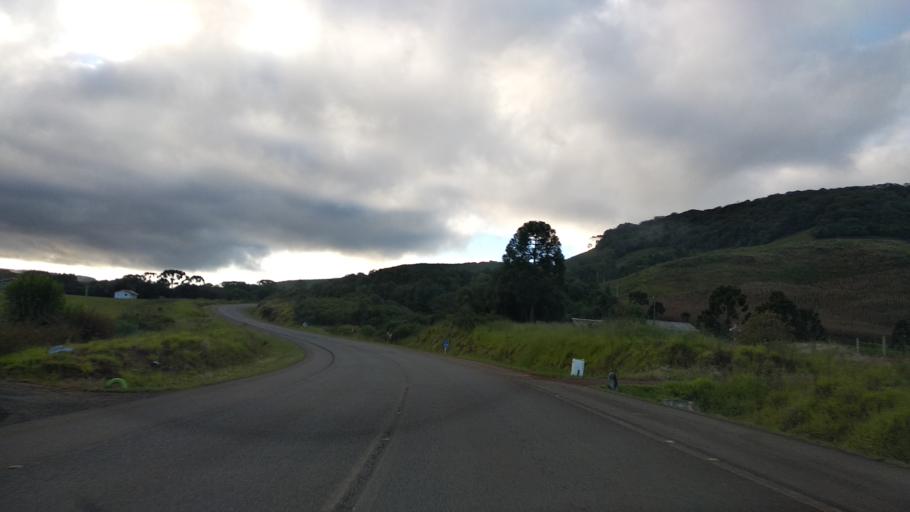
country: BR
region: Santa Catarina
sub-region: Curitibanos
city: Curitibanos
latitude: -27.5746
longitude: -50.8055
